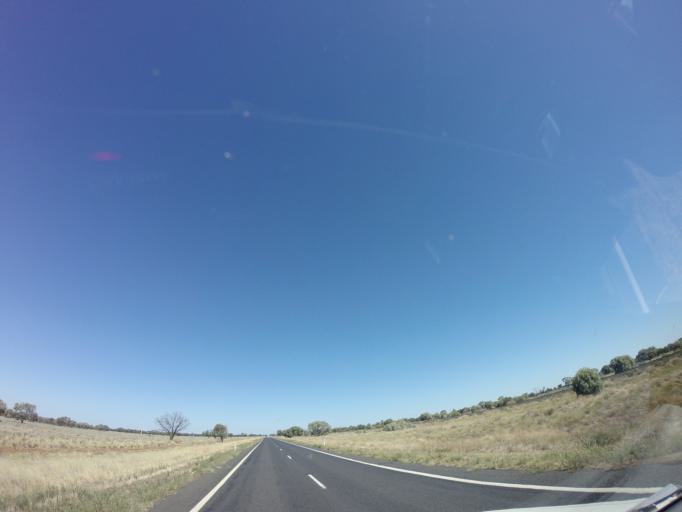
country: AU
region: New South Wales
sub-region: Bogan
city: Nyngan
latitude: -31.6194
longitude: 147.3047
